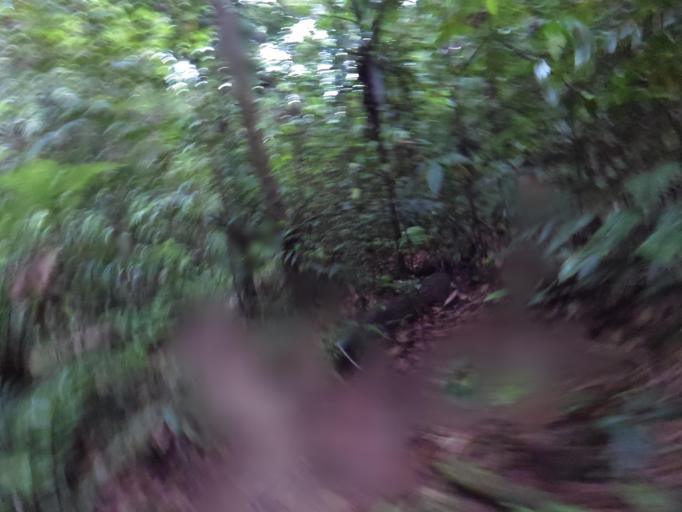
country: FJ
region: Central
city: Suva
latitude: -18.0592
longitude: 178.4697
